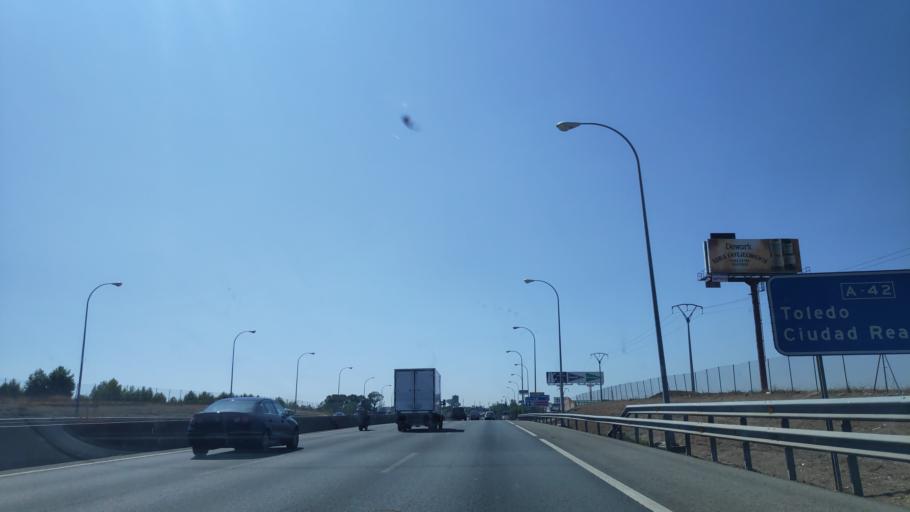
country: ES
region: Madrid
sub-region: Provincia de Madrid
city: Villaverde
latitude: 40.3568
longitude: -3.7219
